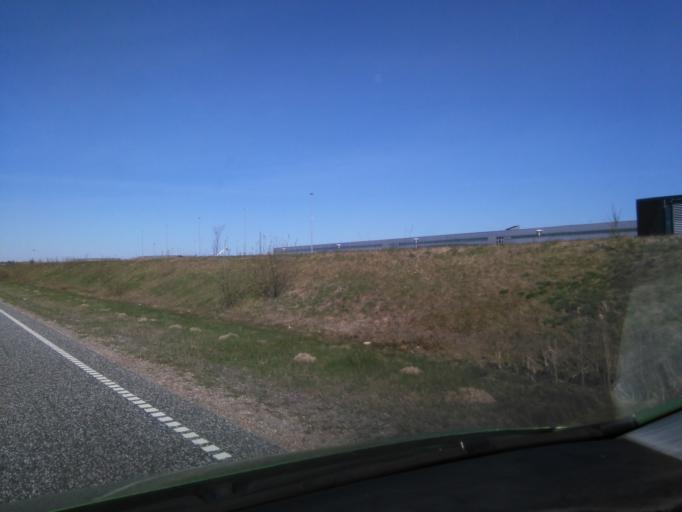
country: DK
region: Central Jutland
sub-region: Hedensted Kommune
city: Torring
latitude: 55.8395
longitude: 9.5997
